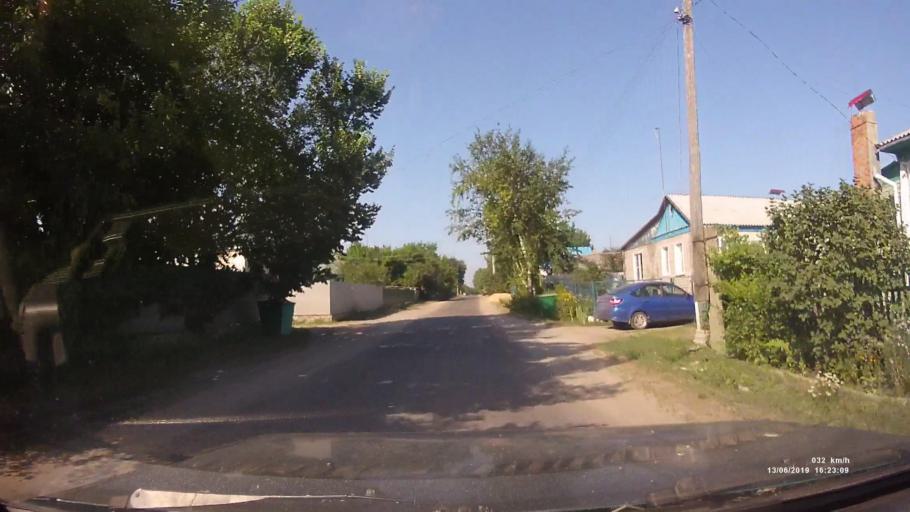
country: RU
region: Rostov
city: Kazanskaya
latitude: 49.7925
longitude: 41.1366
